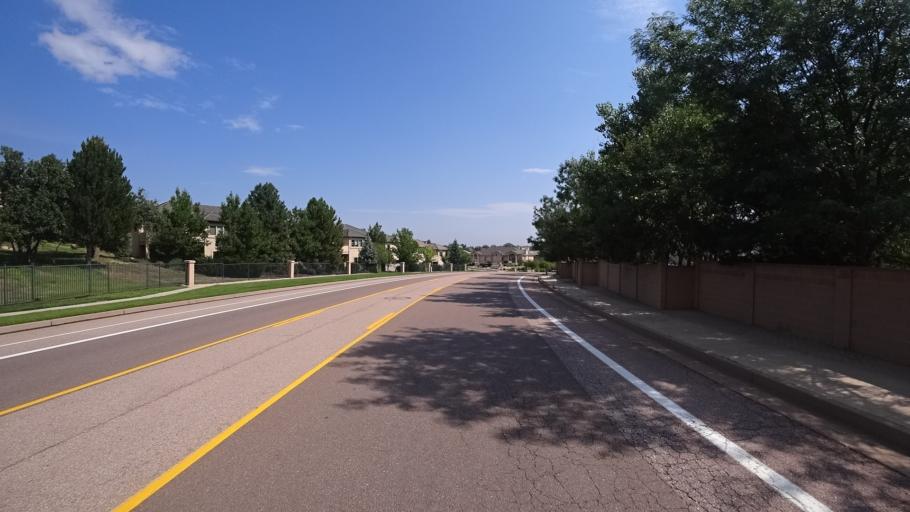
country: US
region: Colorado
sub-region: El Paso County
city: Stratmoor
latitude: 38.7645
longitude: -104.8185
